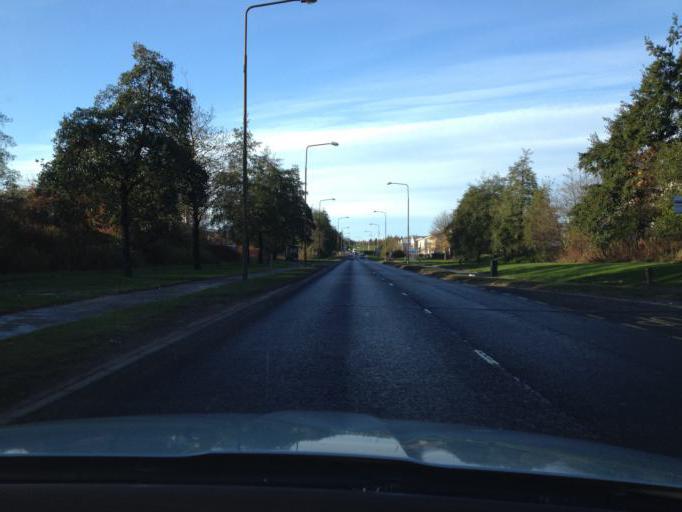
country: GB
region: Scotland
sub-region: West Lothian
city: Livingston
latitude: 55.9085
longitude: -3.5070
